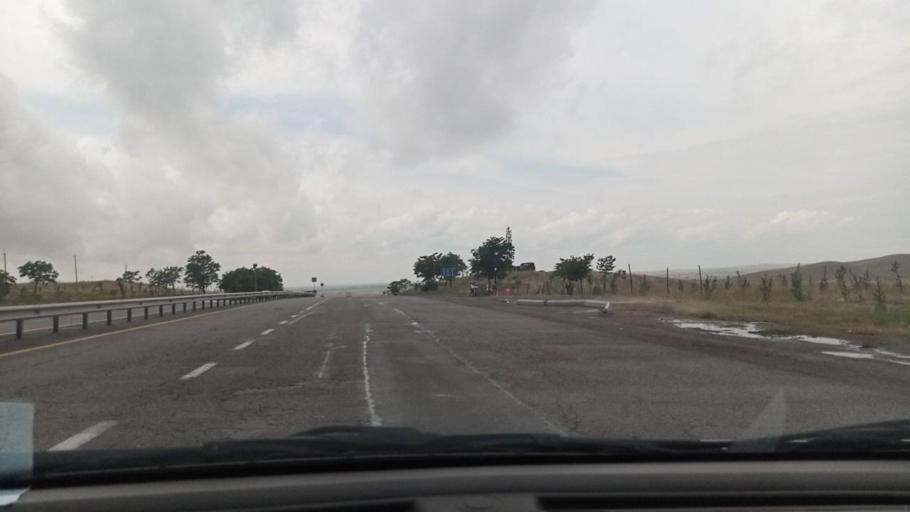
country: UZ
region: Toshkent
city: Ohangaron
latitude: 40.9625
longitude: 69.5564
